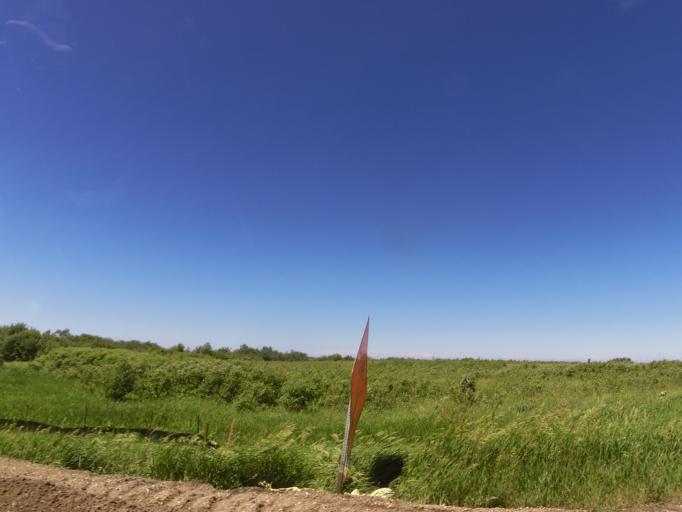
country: US
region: Minnesota
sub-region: Mahnomen County
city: Mahnomen
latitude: 47.1254
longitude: -95.9270
